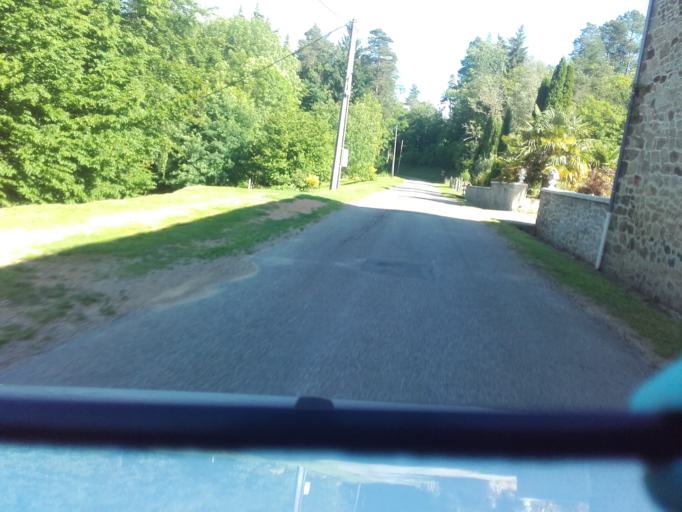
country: FR
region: Limousin
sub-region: Departement de la Correze
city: Laguenne
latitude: 45.2116
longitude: 1.8619
